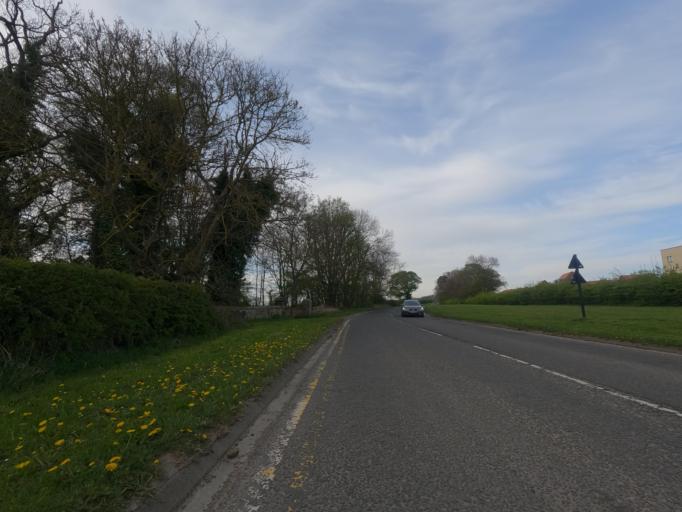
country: GB
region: England
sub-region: Newcastle upon Tyne
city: Dinnington
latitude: 55.0317
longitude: -1.6657
